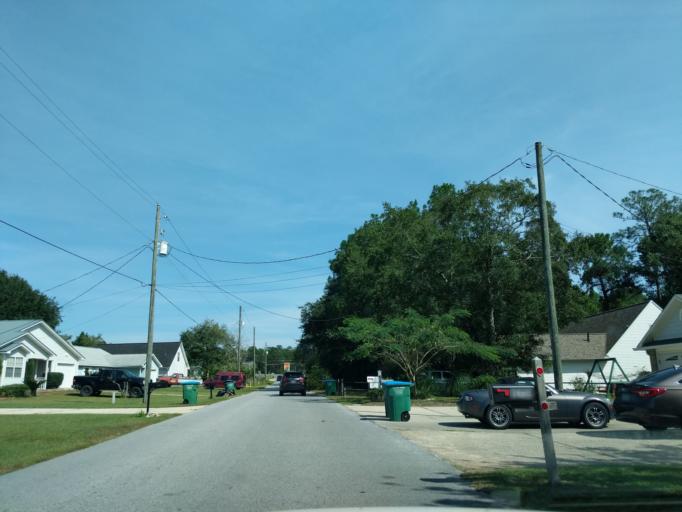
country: US
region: Florida
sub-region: Okaloosa County
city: Crestview
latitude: 30.7001
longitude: -86.5739
